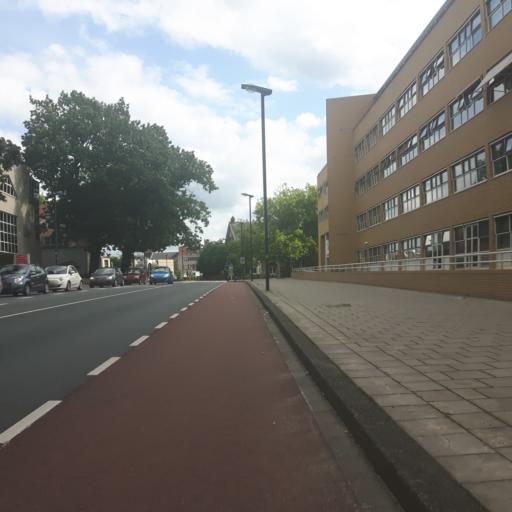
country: NL
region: Overijssel
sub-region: Gemeente Enschede
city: Enschede
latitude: 52.2213
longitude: 6.8873
